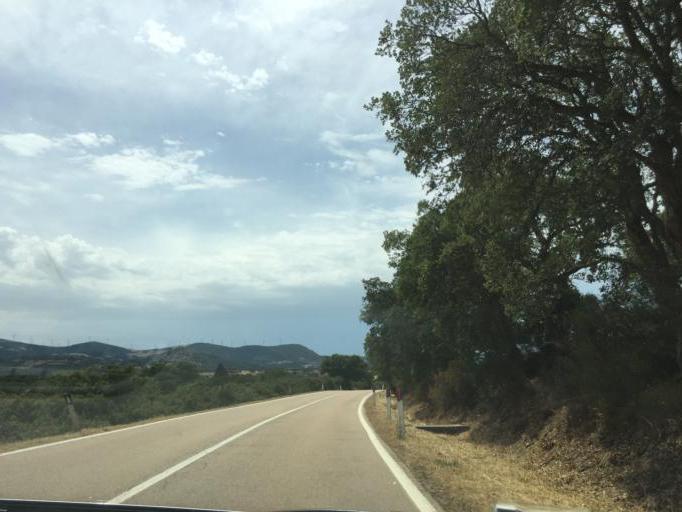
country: IT
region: Sardinia
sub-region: Provincia di Olbia-Tempio
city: Aggius
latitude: 40.9501
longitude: 9.0688
